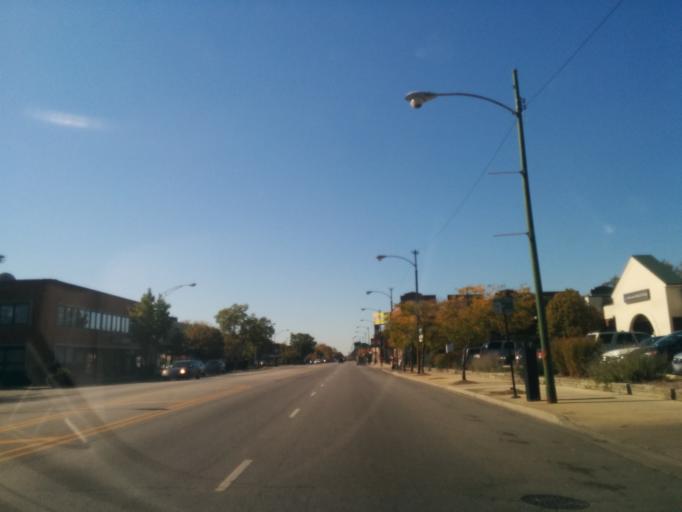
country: US
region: Illinois
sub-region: Cook County
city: Oak Park
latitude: 41.9095
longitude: -87.7850
